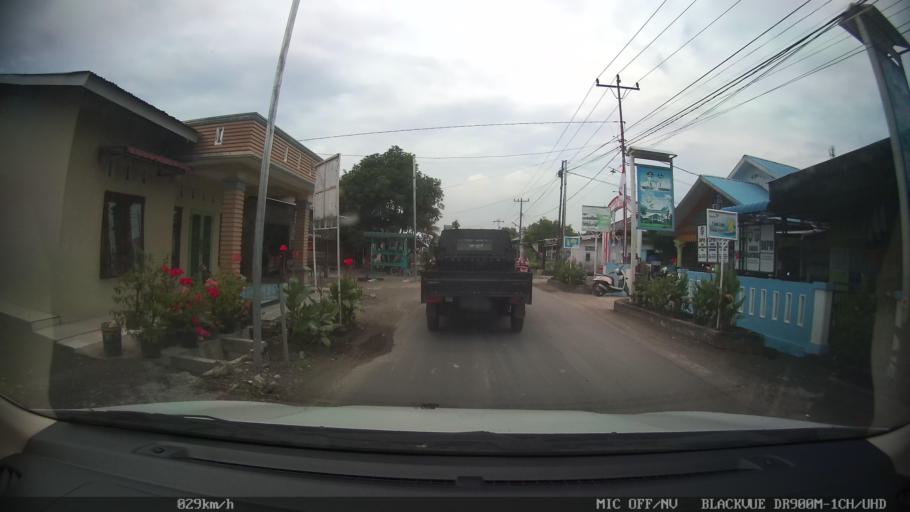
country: ID
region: North Sumatra
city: Binjai
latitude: 3.6307
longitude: 98.5551
